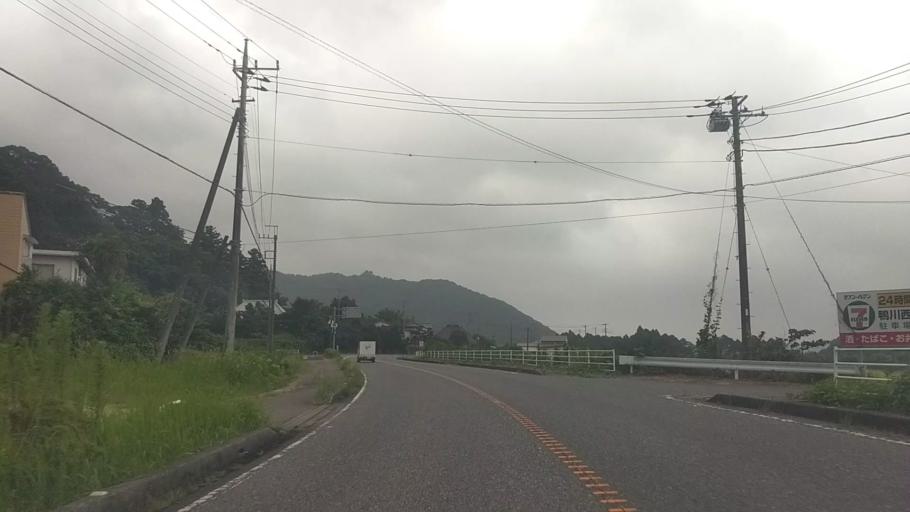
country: JP
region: Chiba
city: Kawaguchi
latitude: 35.1378
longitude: 140.0703
